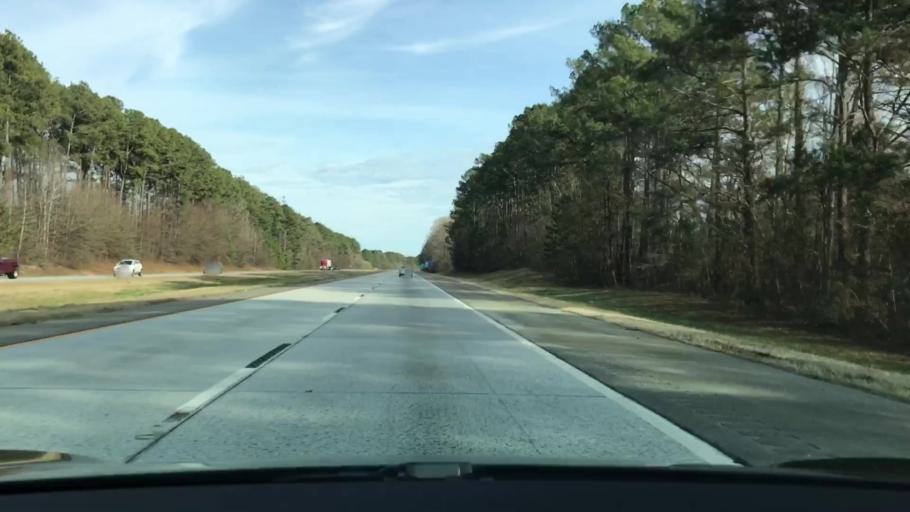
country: US
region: Georgia
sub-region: Morgan County
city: Madison
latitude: 33.5545
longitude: -83.3859
